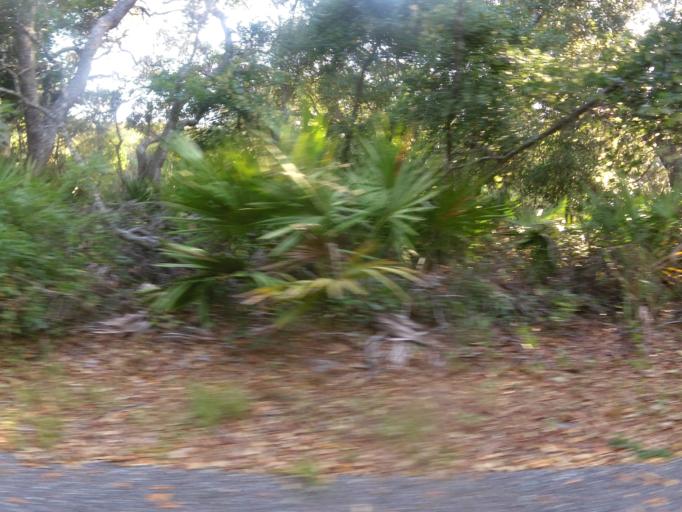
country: US
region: Florida
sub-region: Duval County
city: Atlantic Beach
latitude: 30.4983
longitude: -81.4479
